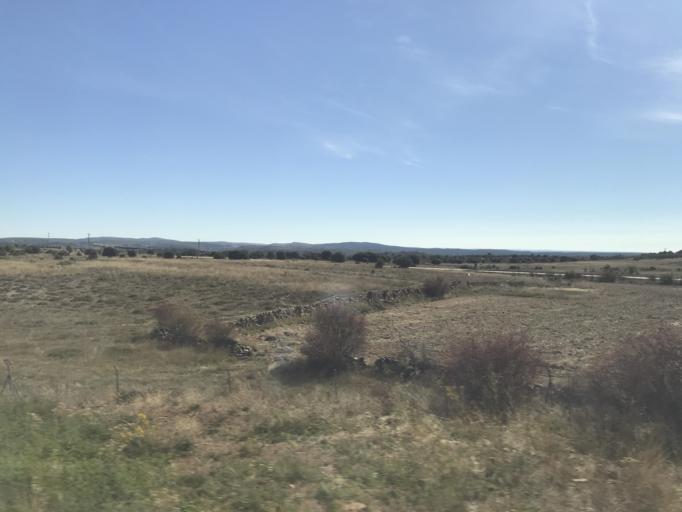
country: ES
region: Castille-La Mancha
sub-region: Provincia de Guadalajara
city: Alcolea del Pinar
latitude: 41.0419
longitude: -2.4438
